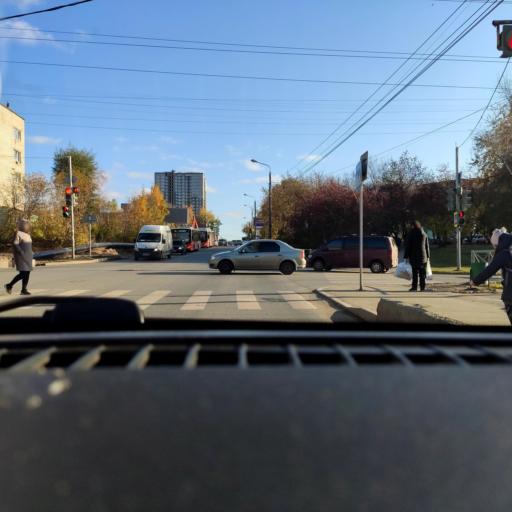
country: RU
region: Perm
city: Kondratovo
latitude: 57.9706
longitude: 56.1715
